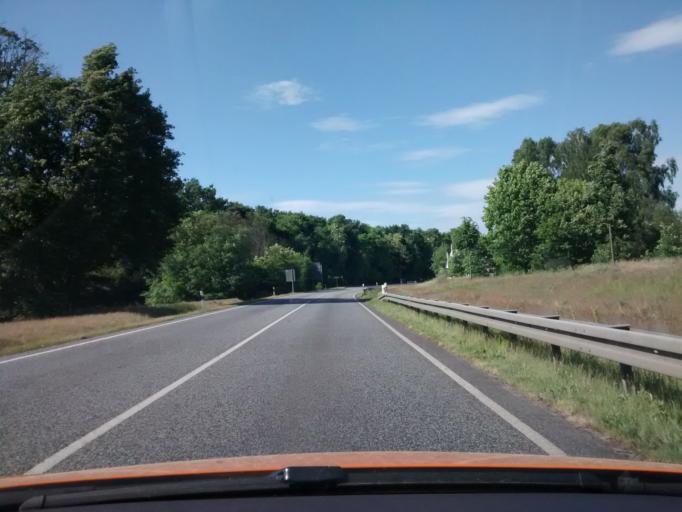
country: DE
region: Brandenburg
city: Juterbog
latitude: 52.0100
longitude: 13.0968
